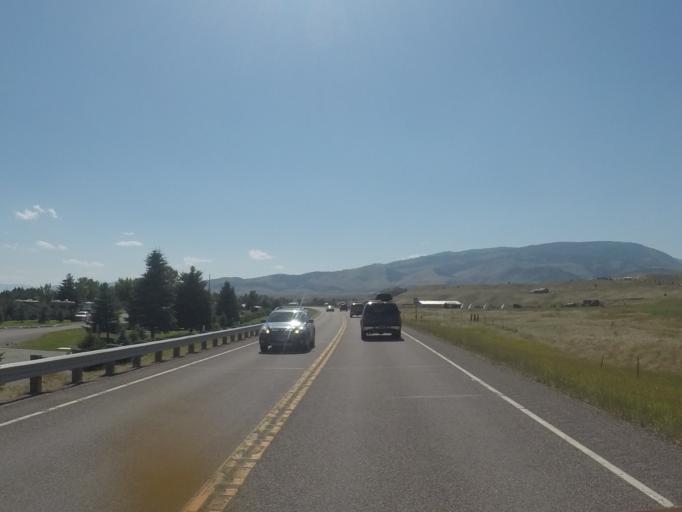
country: US
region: Montana
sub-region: Park County
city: Livingston
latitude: 45.4186
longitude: -110.6797
